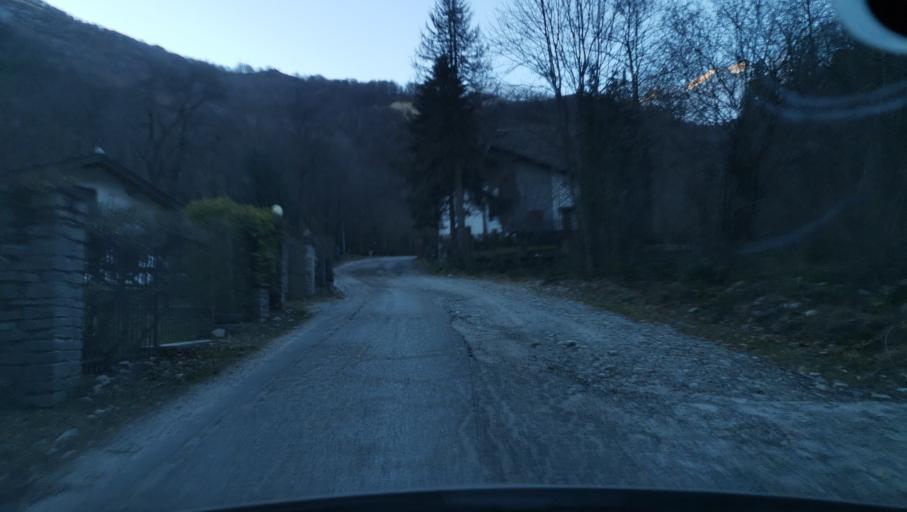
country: IT
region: Piedmont
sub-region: Provincia di Torino
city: Rora
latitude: 44.7708
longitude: 7.2049
